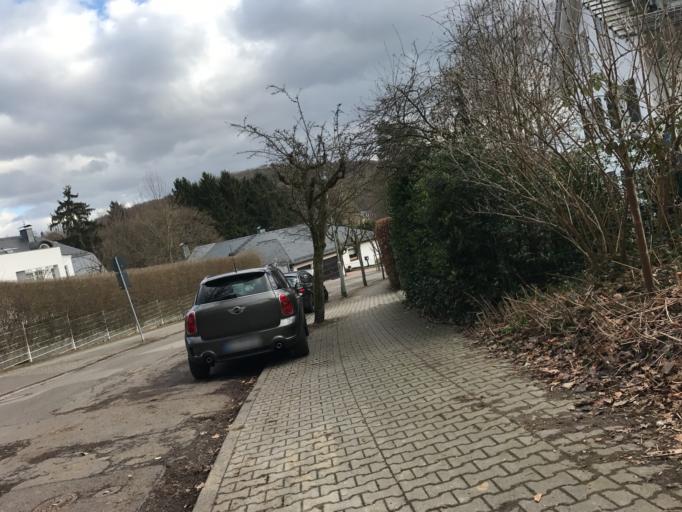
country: DE
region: Hesse
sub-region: Regierungsbezirk Darmstadt
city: Konigstein im Taunus
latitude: 50.1947
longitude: 8.4667
